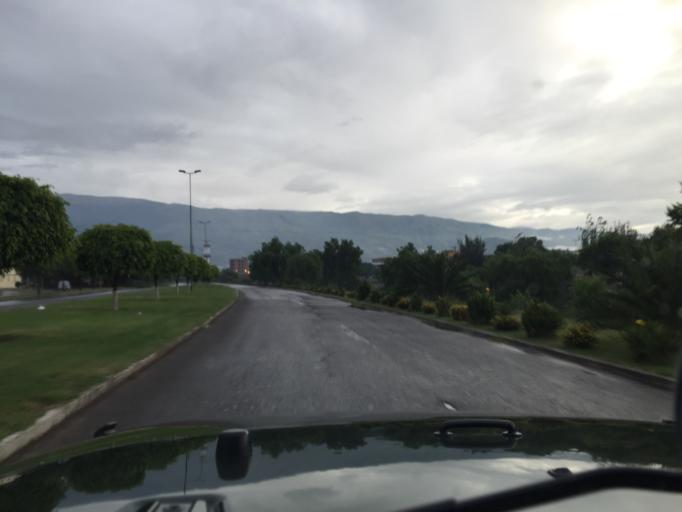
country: BO
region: Cochabamba
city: Cochabamba
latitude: -17.4052
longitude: -66.1710
